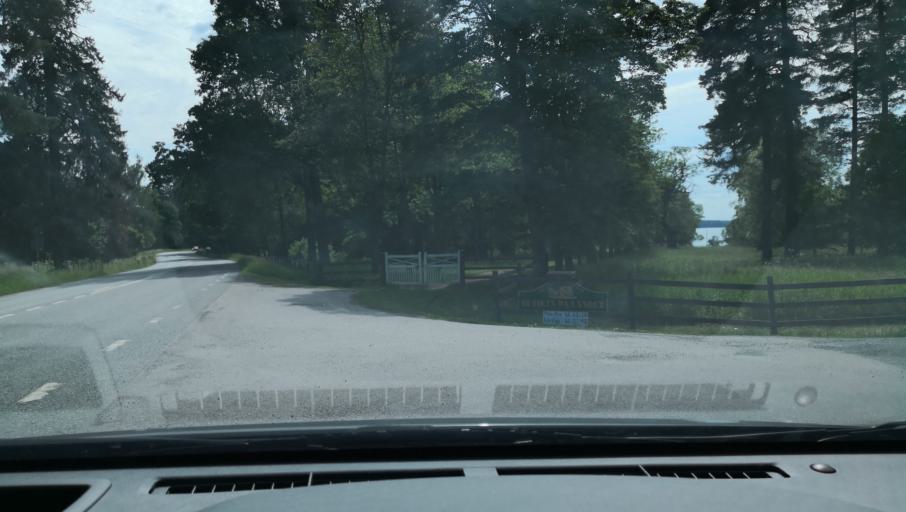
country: SE
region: Uppsala
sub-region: Uppsala Kommun
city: Saevja
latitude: 59.7645
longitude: 17.6461
